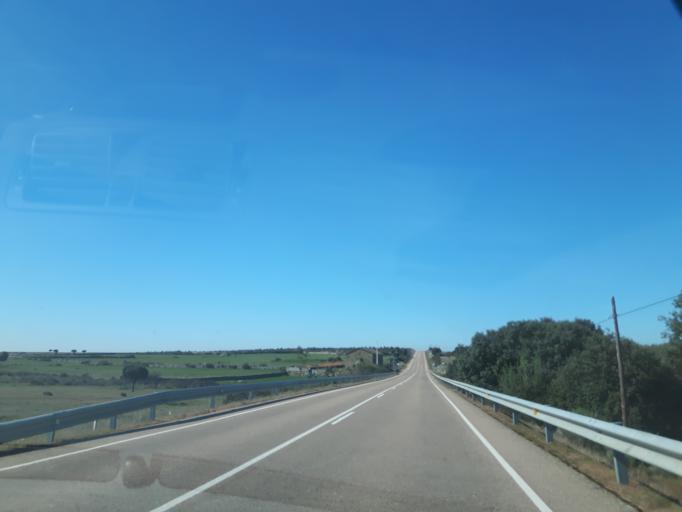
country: ES
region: Castille and Leon
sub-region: Provincia de Salamanca
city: Guadramiro
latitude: 41.0103
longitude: -6.4923
